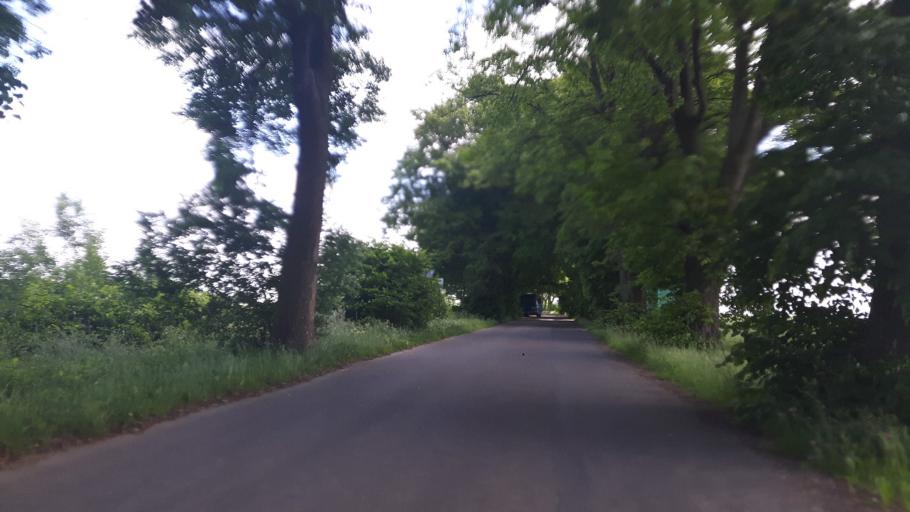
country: PL
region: West Pomeranian Voivodeship
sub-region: Powiat slawienski
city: Slawno
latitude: 54.5089
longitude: 16.5799
